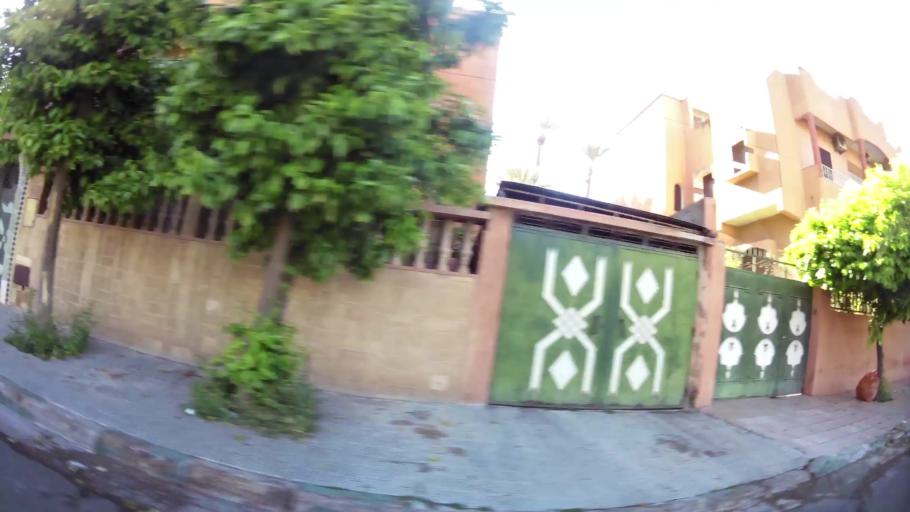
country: MA
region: Marrakech-Tensift-Al Haouz
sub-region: Marrakech
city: Marrakesh
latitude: 31.6505
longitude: -8.0197
